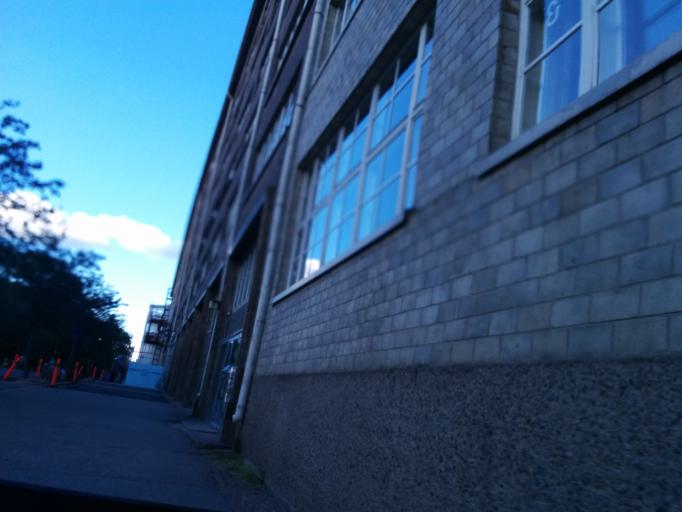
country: FI
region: Uusimaa
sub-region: Helsinki
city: Helsinki
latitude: 60.2092
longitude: 24.9760
